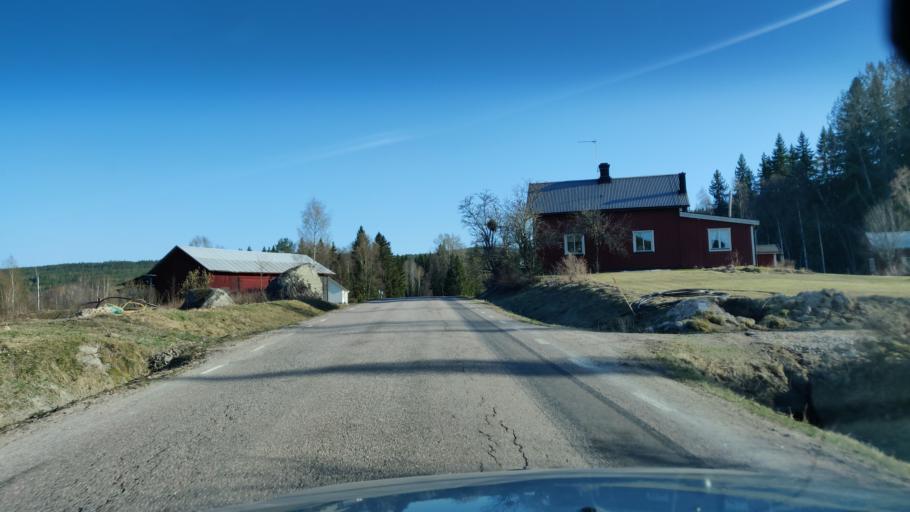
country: SE
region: Vaermland
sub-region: Munkfors Kommun
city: Munkfors
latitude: 59.9765
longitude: 13.4131
